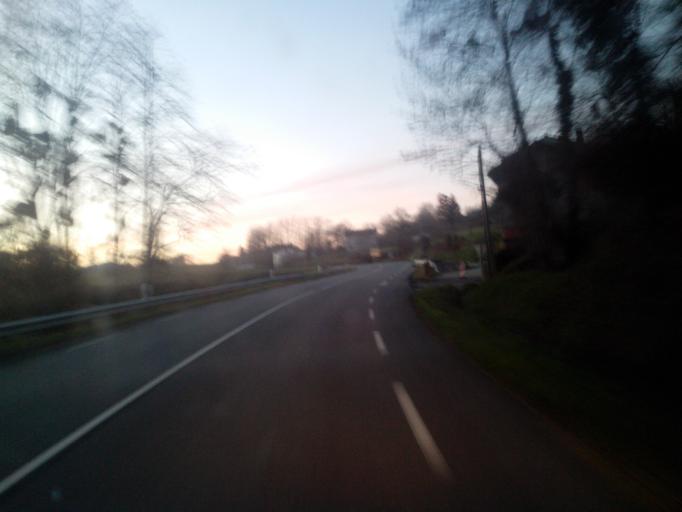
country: FR
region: Midi-Pyrenees
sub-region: Departement de l'Ariege
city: Foix
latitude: 42.9680
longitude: 1.5936
